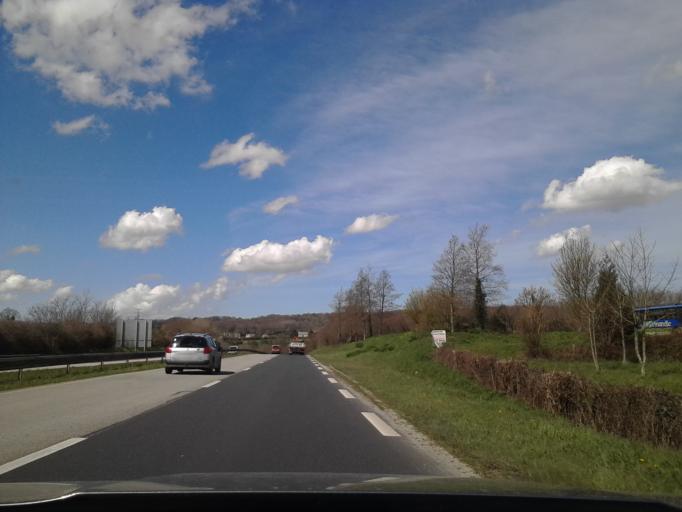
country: FR
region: Lower Normandy
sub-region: Departement de la Manche
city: Brix
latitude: 49.5366
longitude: -1.5365
